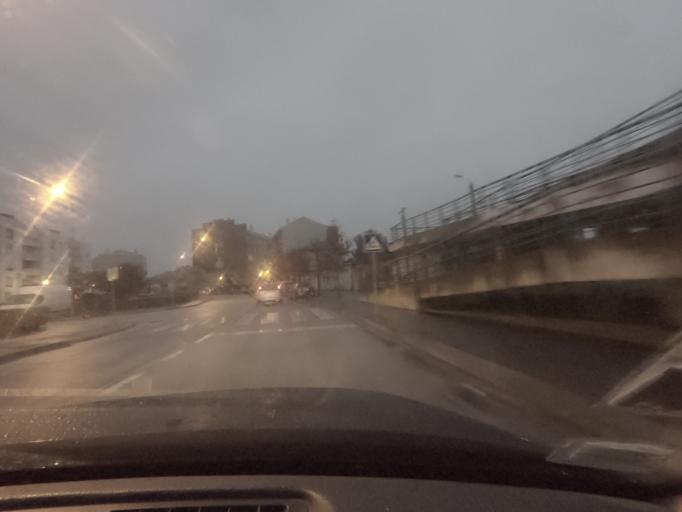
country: PT
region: Porto
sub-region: Matosinhos
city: Guifoes
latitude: 41.1880
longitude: -8.6665
